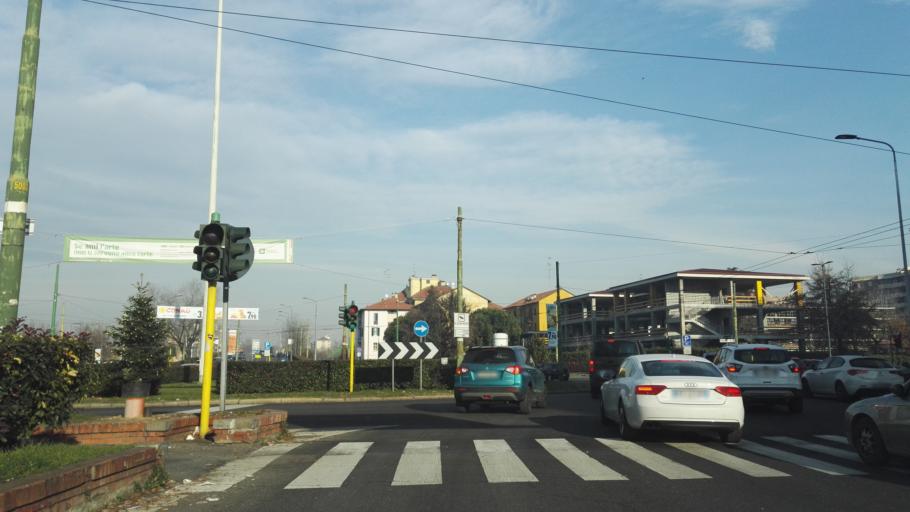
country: IT
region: Lombardy
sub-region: Citta metropolitana di Milano
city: Chiaravalle
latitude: 45.4439
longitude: 9.2242
